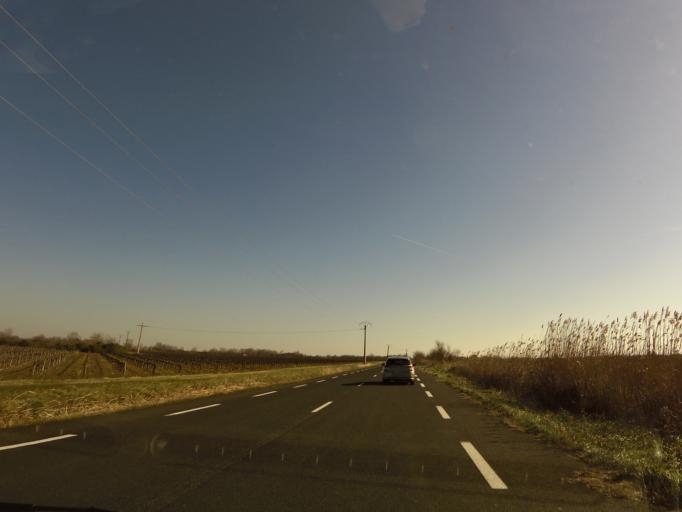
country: FR
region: Languedoc-Roussillon
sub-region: Departement du Gard
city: Aigues-Mortes
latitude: 43.5673
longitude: 4.3119
